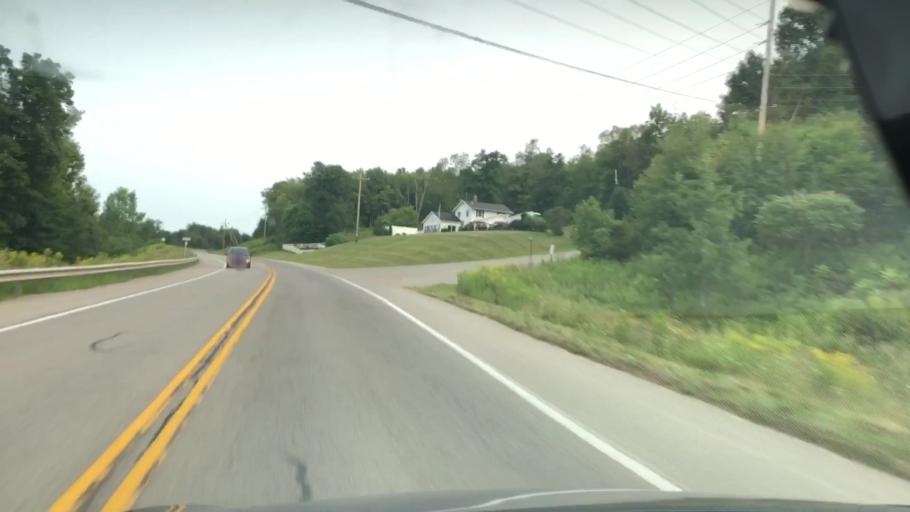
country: US
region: Pennsylvania
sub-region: Venango County
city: Hasson Heights
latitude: 41.5283
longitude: -79.7138
